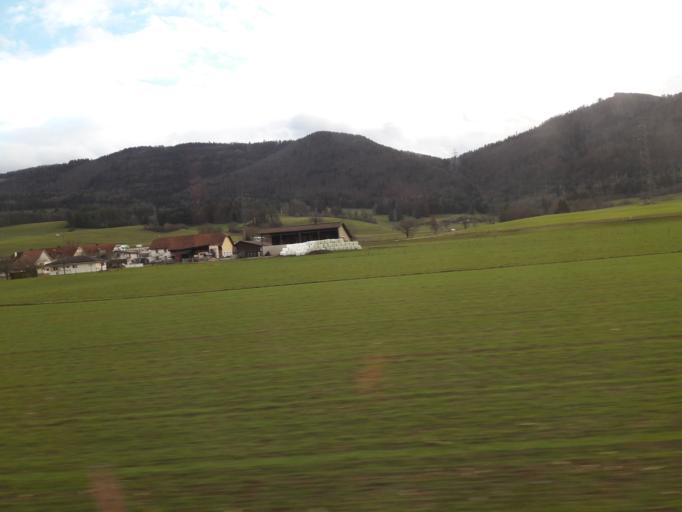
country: CH
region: Jura
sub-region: Delemont District
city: Courfaivre
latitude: 47.3368
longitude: 7.2690
